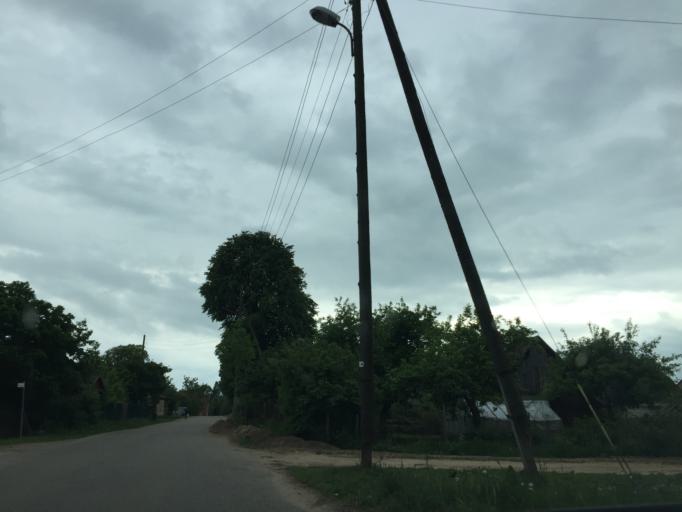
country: LV
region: Aglona
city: Aglona
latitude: 56.0562
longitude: 26.7922
